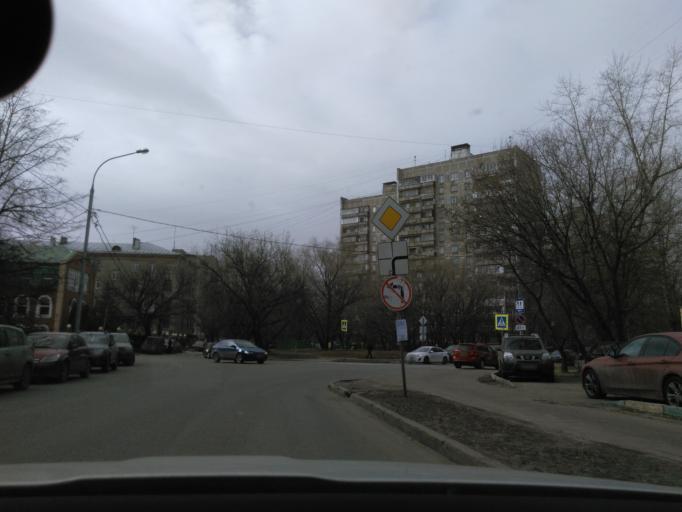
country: RU
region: Moskovskaya
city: Koptevo
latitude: 55.8192
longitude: 37.5180
